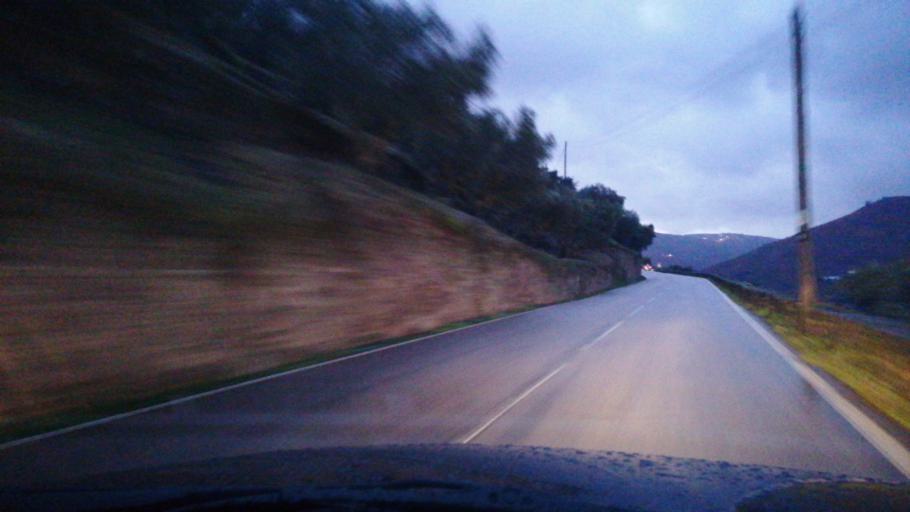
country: PT
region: Viseu
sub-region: Tabuaco
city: Tabuaco
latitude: 41.1713
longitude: -7.5566
